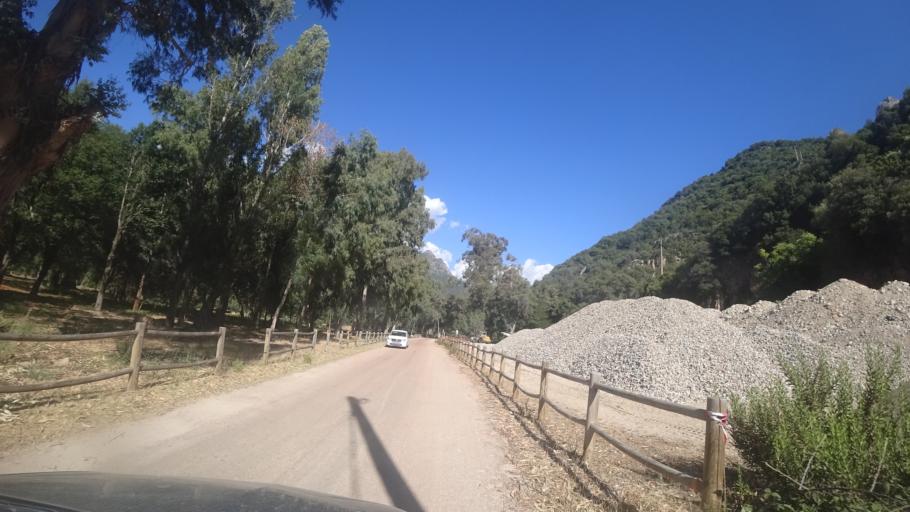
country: FR
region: Corsica
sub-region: Departement de la Corse-du-Sud
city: Cargese
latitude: 42.2641
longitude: 8.6942
